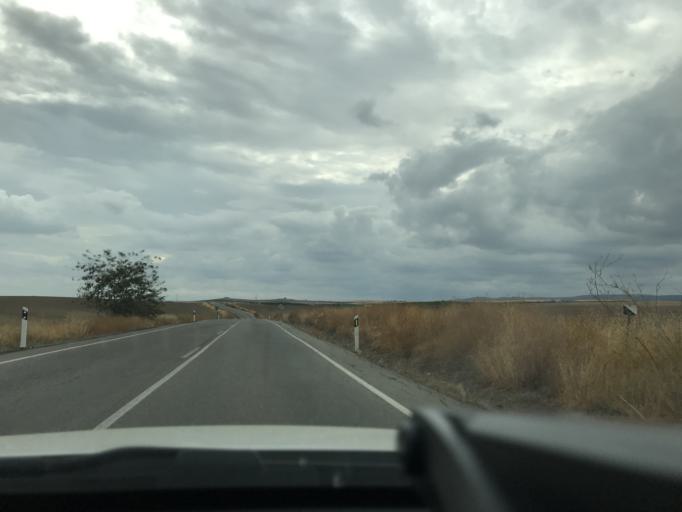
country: ES
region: Andalusia
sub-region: Provincia de Sevilla
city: Tocina
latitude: 37.6321
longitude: -5.7674
